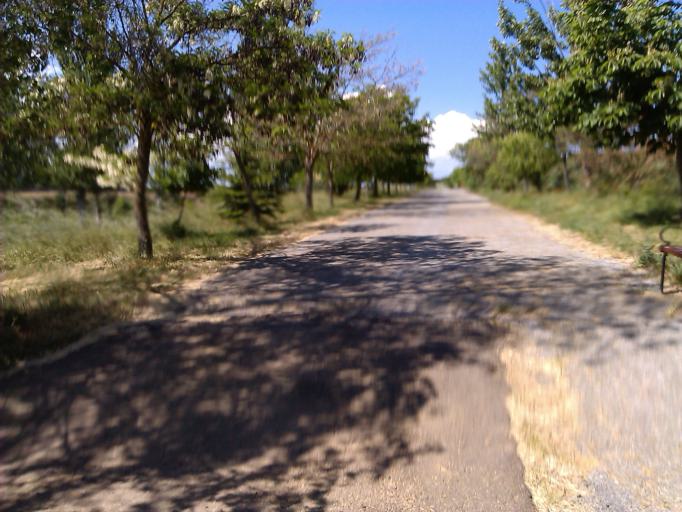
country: ES
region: Castille and Leon
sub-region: Provincia de Palencia
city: Ledigos
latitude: 42.3563
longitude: -4.8651
